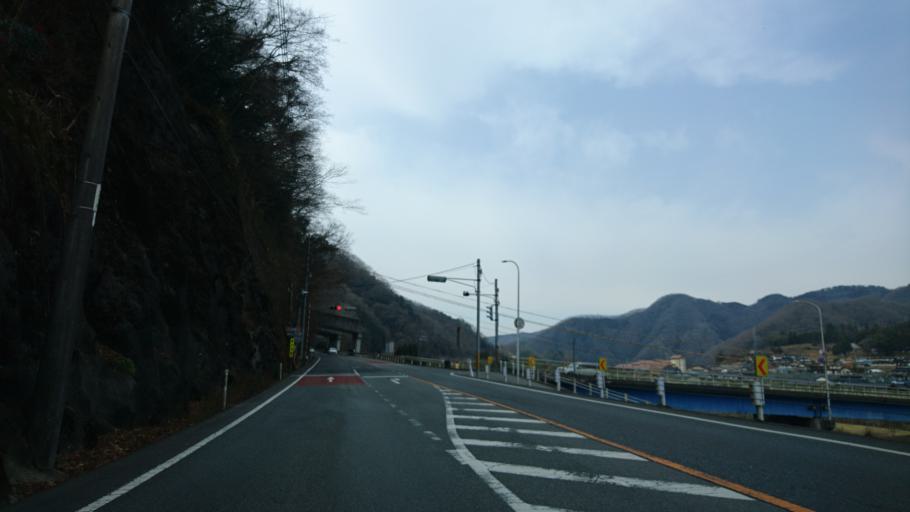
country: JP
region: Okayama
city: Takahashi
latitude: 34.8461
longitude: 133.5932
